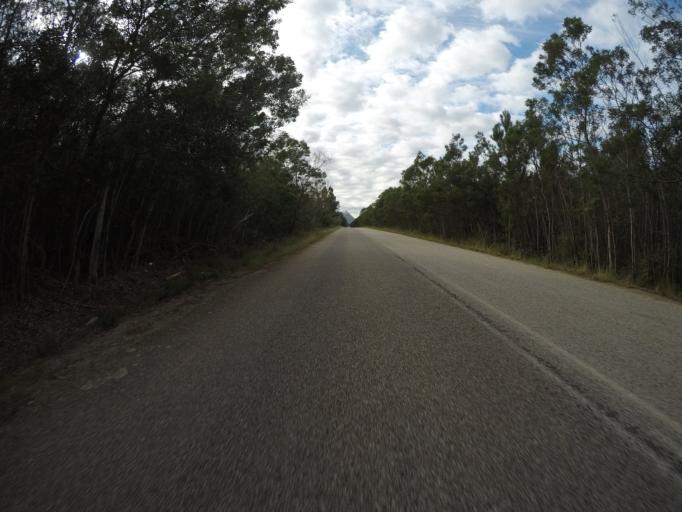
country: ZA
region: Eastern Cape
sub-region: Cacadu District Municipality
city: Kareedouw
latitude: -34.0162
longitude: 24.3337
